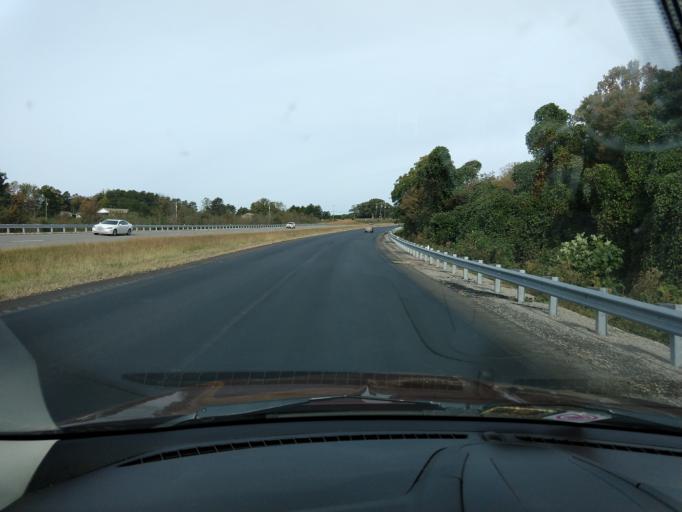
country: US
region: Virginia
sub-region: Pittsylvania County
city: Chatham
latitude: 36.8693
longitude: -79.4078
